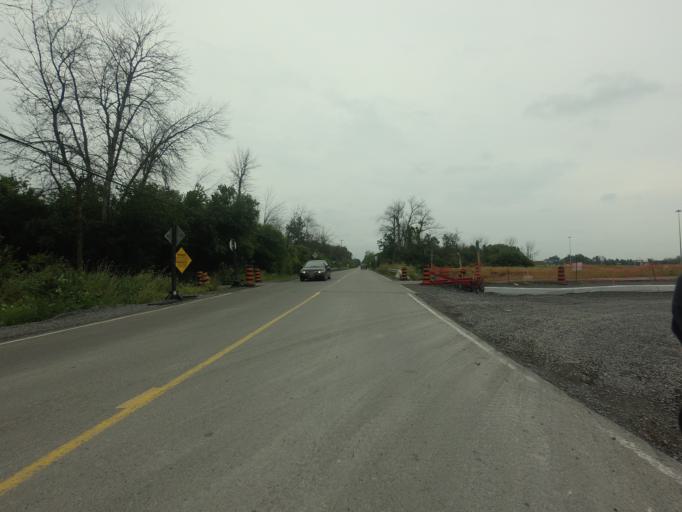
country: CA
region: Ontario
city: Bells Corners
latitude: 45.3414
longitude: -75.8372
